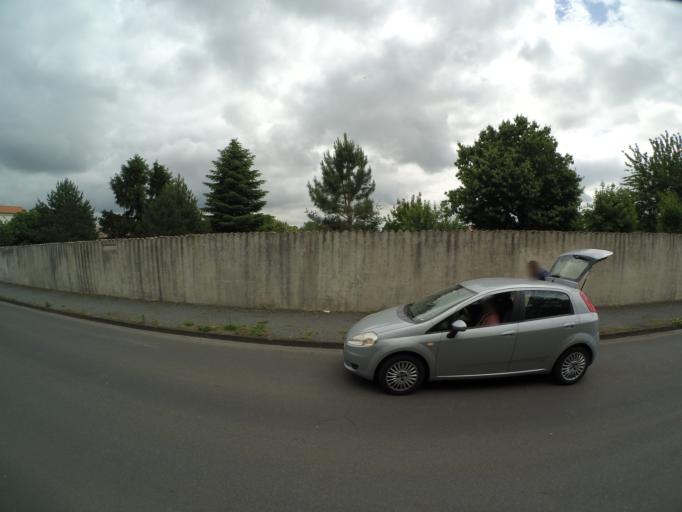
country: FR
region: Poitou-Charentes
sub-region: Departement de la Charente-Maritime
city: Breuil-Magne
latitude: 45.9588
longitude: -0.9695
